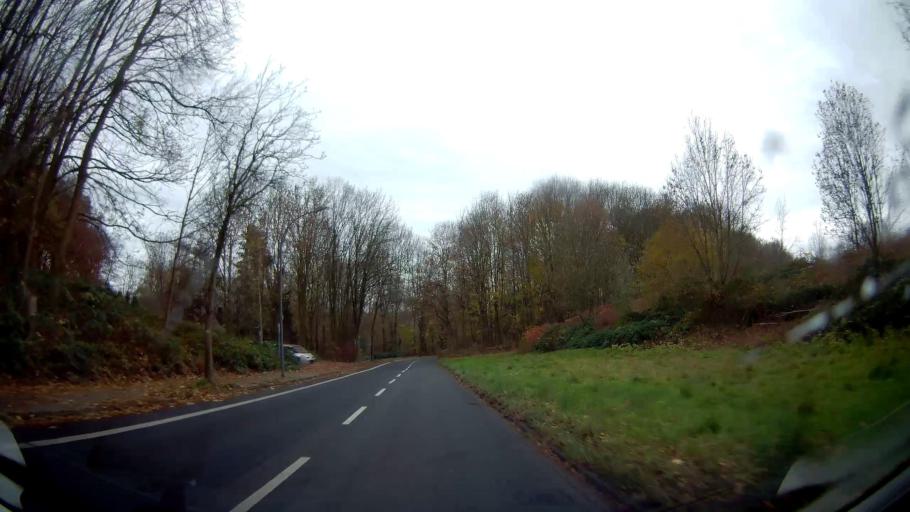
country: DE
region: North Rhine-Westphalia
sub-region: Regierungsbezirk Arnsberg
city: Bochum
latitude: 51.5027
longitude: 7.2308
